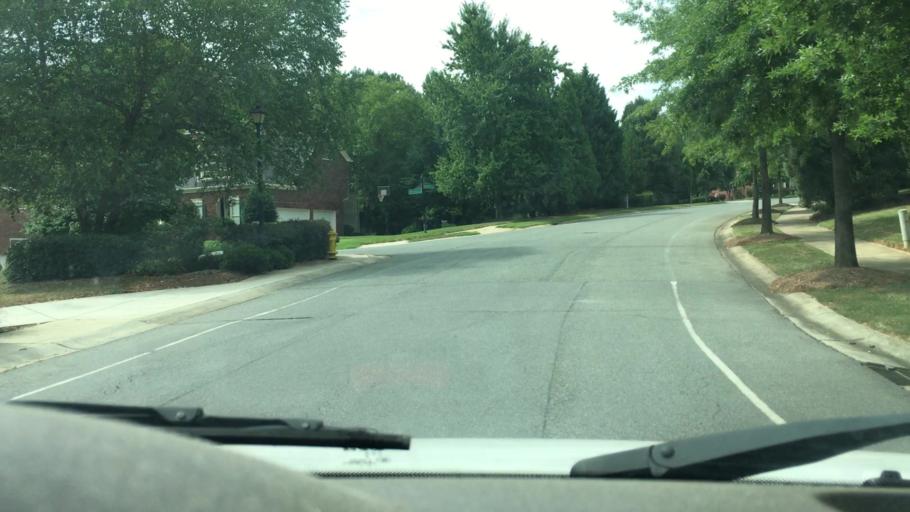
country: US
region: North Carolina
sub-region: Gaston County
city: Davidson
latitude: 35.4642
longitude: -80.7838
